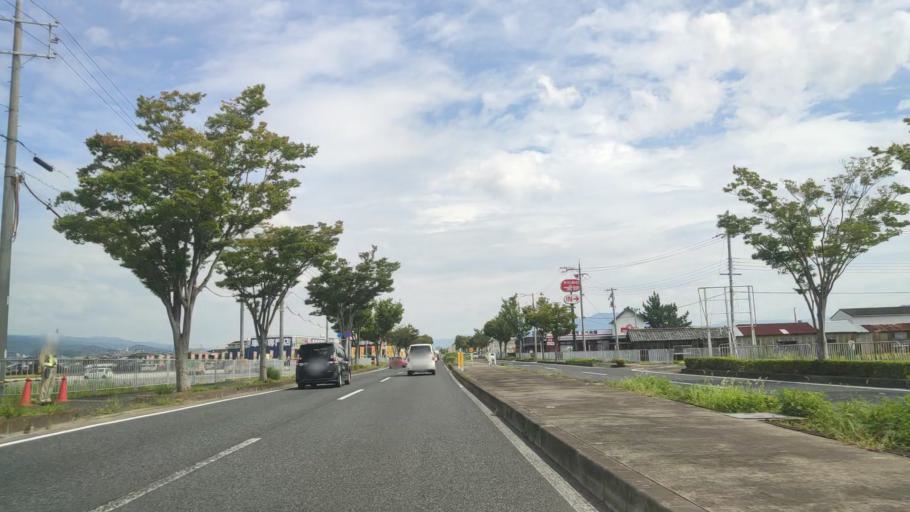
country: JP
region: Wakayama
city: Iwade
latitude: 34.2639
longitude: 135.2717
